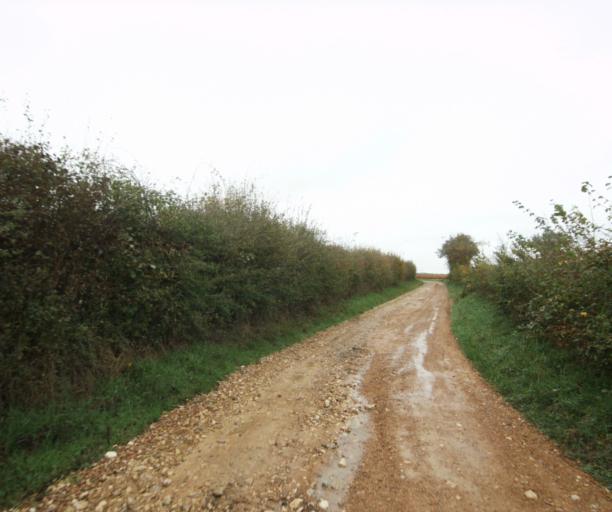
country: FR
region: Bourgogne
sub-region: Departement de Saone-et-Loire
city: Tournus
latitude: 46.4849
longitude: 4.8633
